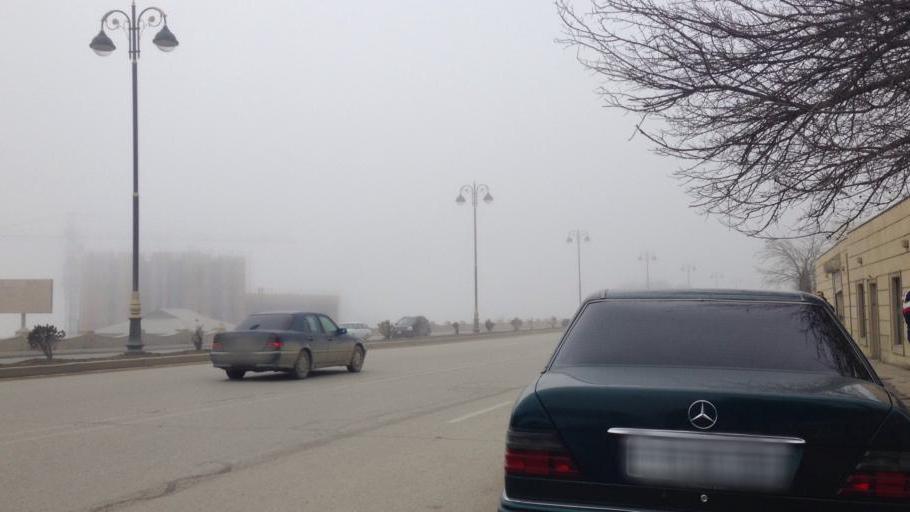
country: AZ
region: Baki
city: Qaracuxur
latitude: 40.3538
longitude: 49.9560
